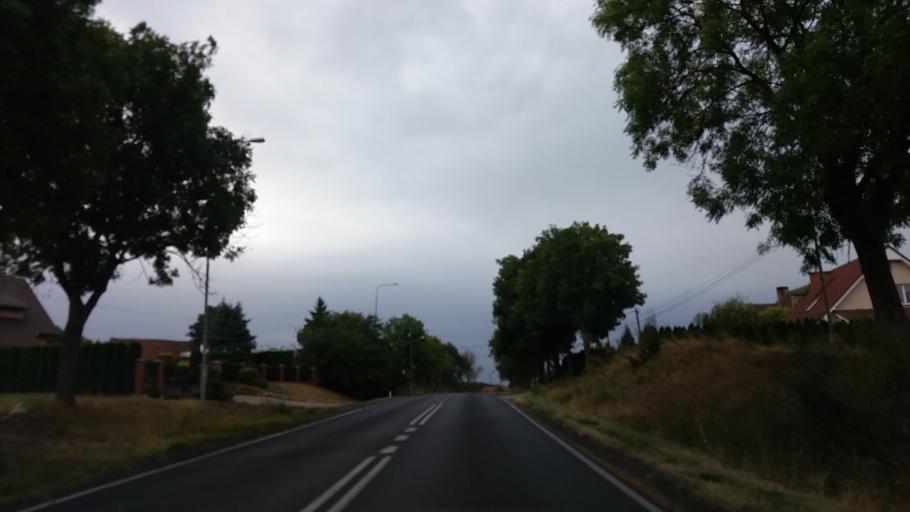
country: PL
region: West Pomeranian Voivodeship
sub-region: Powiat mysliborski
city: Barlinek
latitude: 52.9685
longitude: 15.1855
